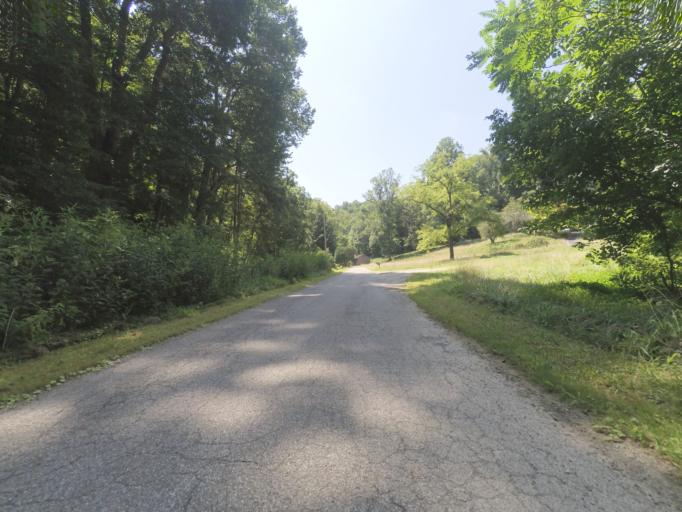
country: US
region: West Virginia
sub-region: Cabell County
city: Huntington
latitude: 38.3858
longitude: -82.4487
